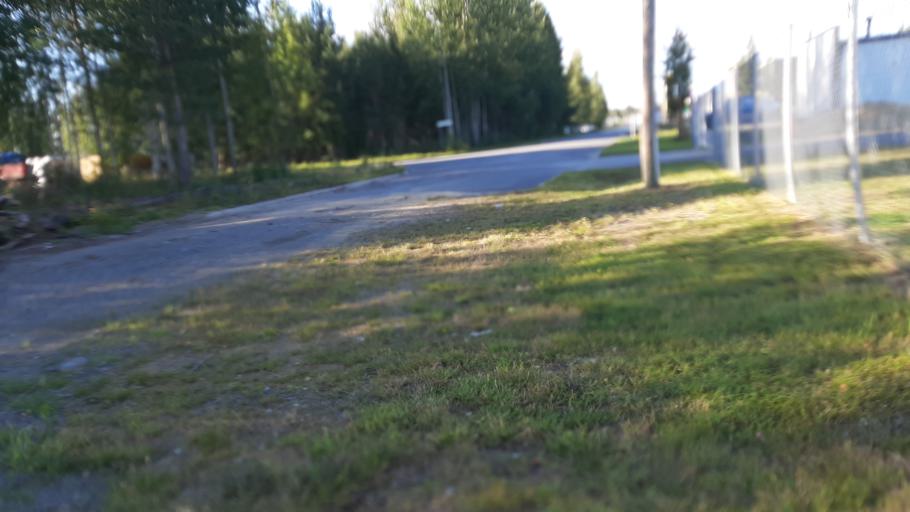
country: FI
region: North Karelia
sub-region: Joensuu
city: Joensuu
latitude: 62.6262
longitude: 29.7499
